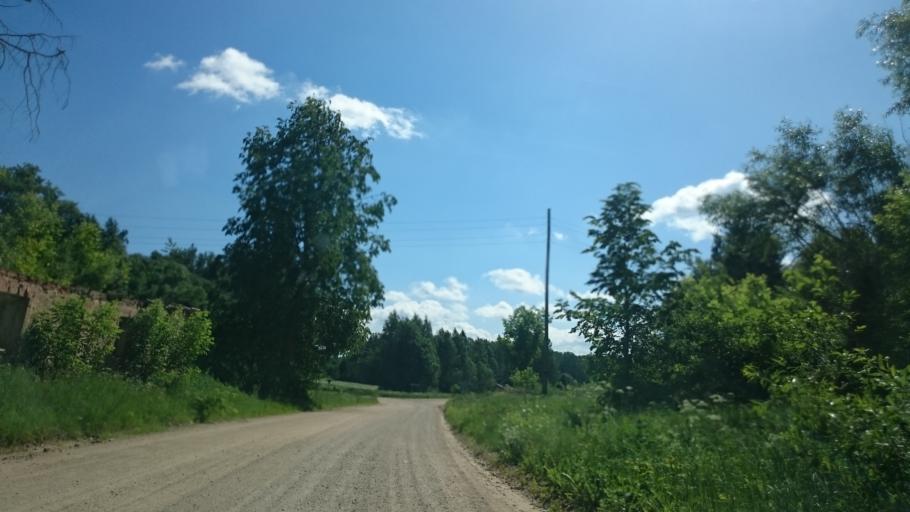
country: LV
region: Cibla
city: Cibla
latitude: 56.5404
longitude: 27.9476
